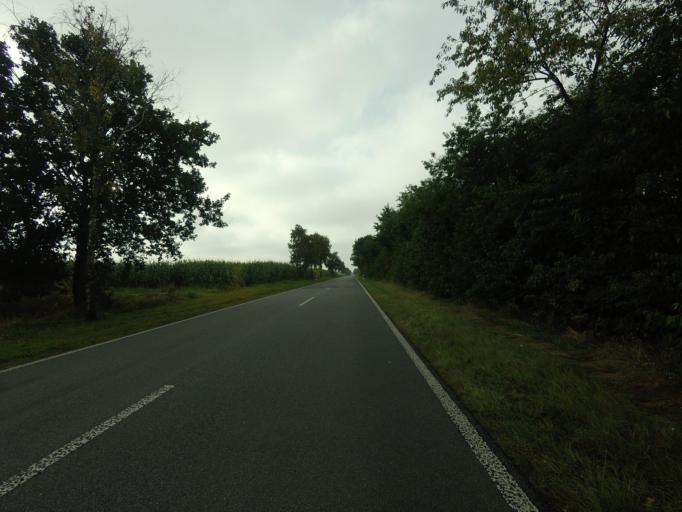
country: DE
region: Lower Saxony
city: Wielen
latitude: 52.5057
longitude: 6.7354
